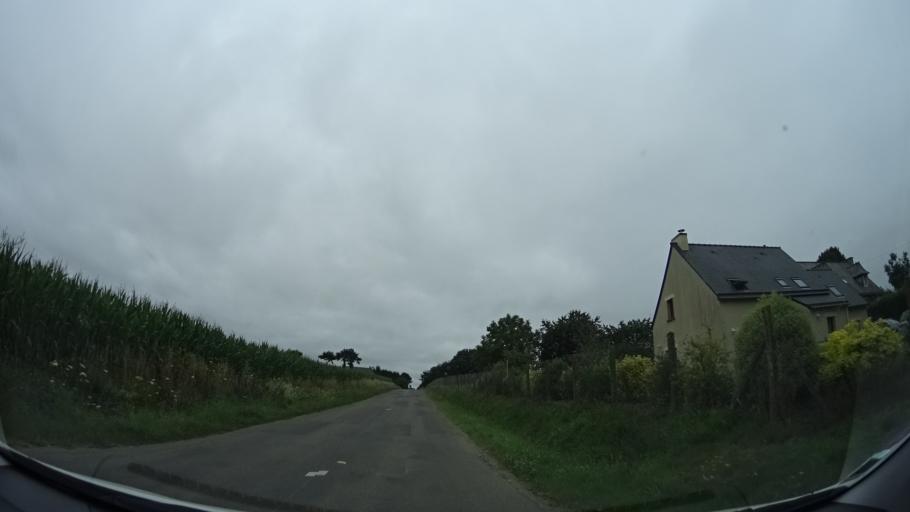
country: FR
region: Brittany
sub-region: Departement des Cotes-d'Armor
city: Evran
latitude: 48.3317
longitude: -1.9328
